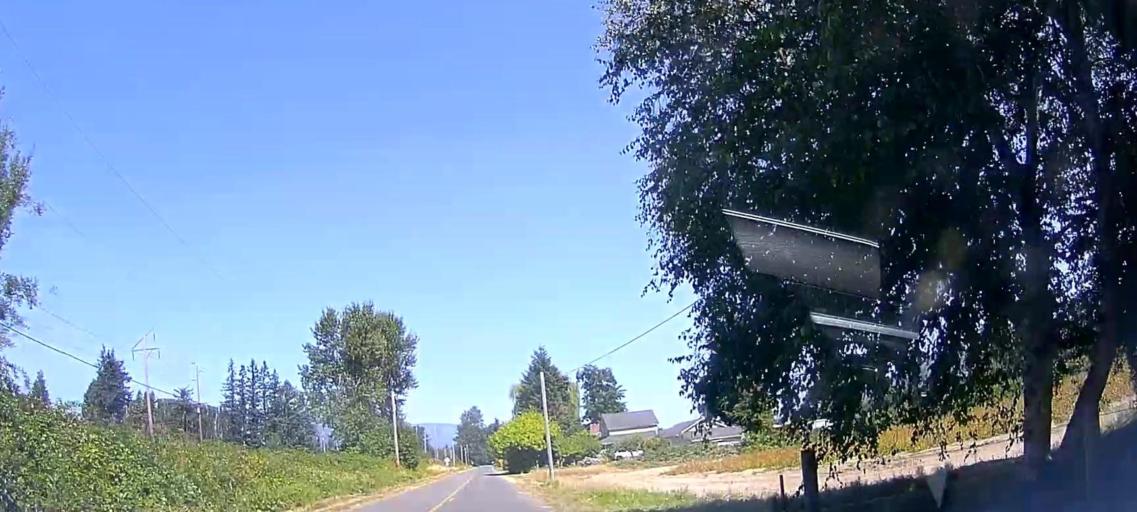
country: US
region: Washington
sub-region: Skagit County
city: Burlington
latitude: 48.4864
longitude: -122.2954
